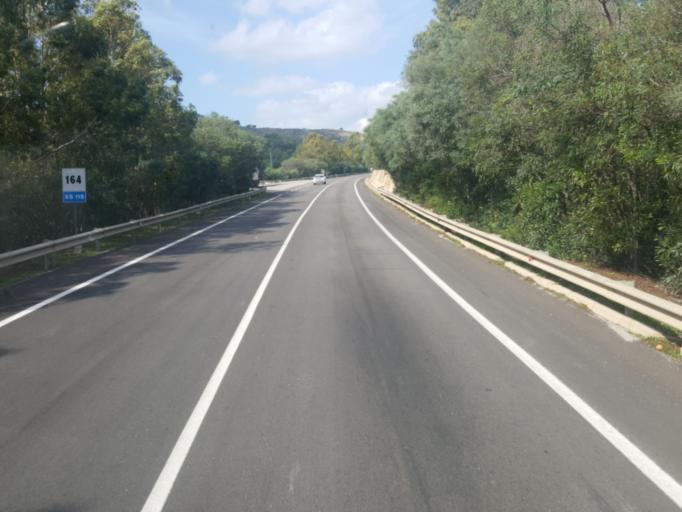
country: IT
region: Sicily
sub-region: Agrigento
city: Siculiana
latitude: 37.3481
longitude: 13.3832
